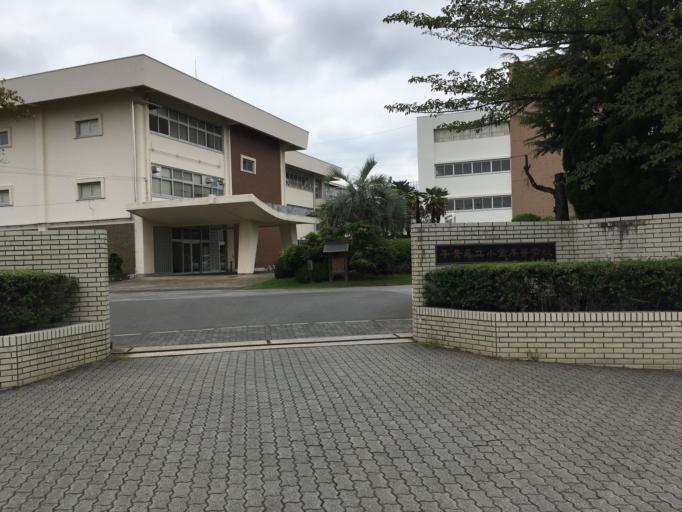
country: JP
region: Chiba
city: Nagareyama
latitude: 35.8336
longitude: 139.9134
